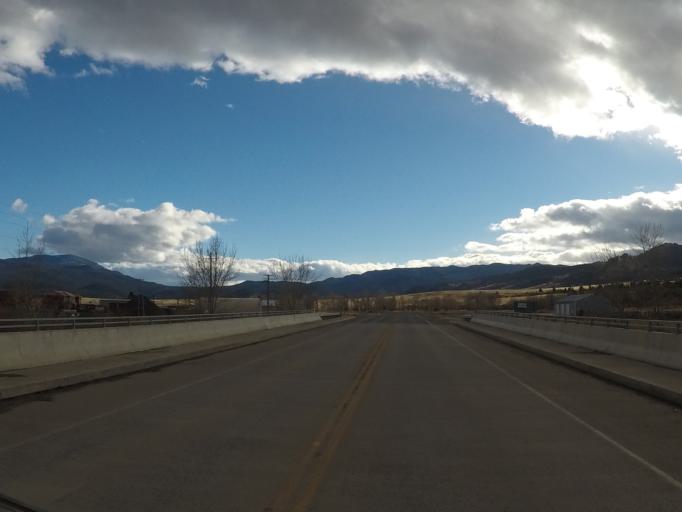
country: US
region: Montana
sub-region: Jefferson County
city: Boulder
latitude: 46.2318
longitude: -112.1211
